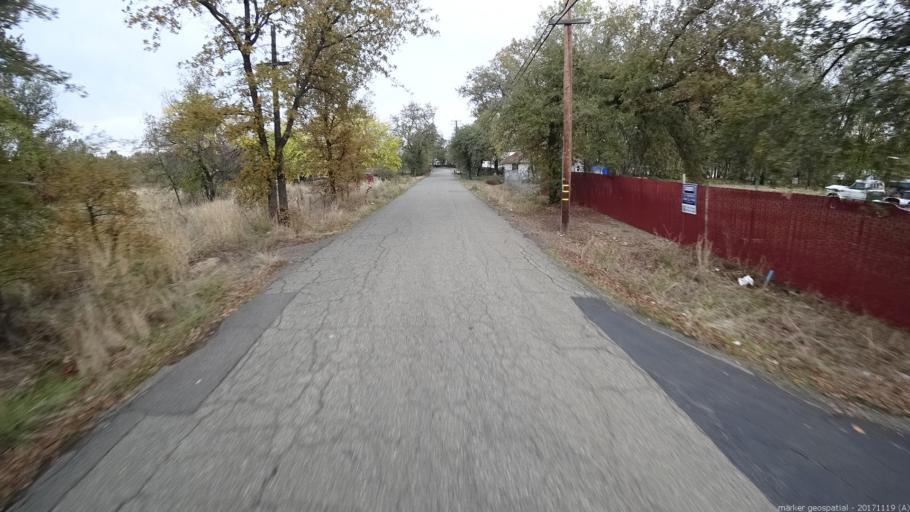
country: US
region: California
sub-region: Shasta County
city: Anderson
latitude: 40.4895
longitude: -122.3667
